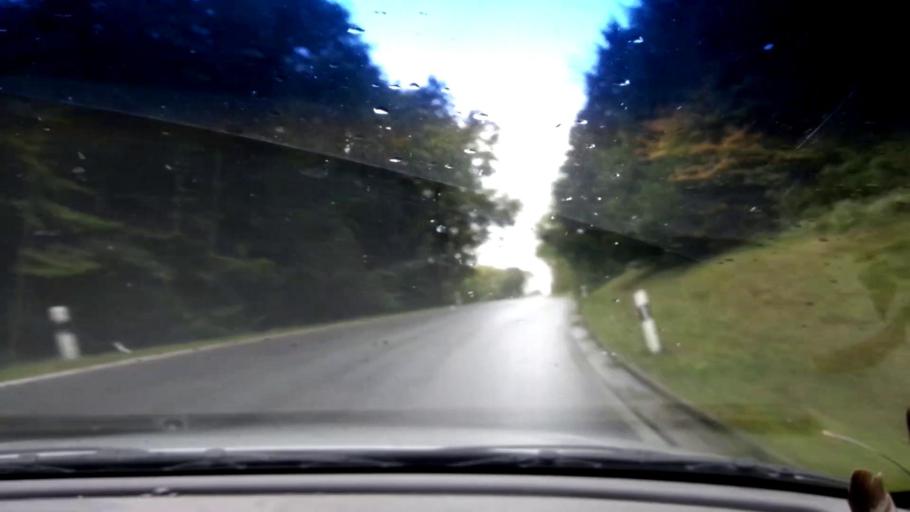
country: DE
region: Bavaria
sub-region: Upper Franconia
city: Poxdorf
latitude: 49.8776
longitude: 11.0976
